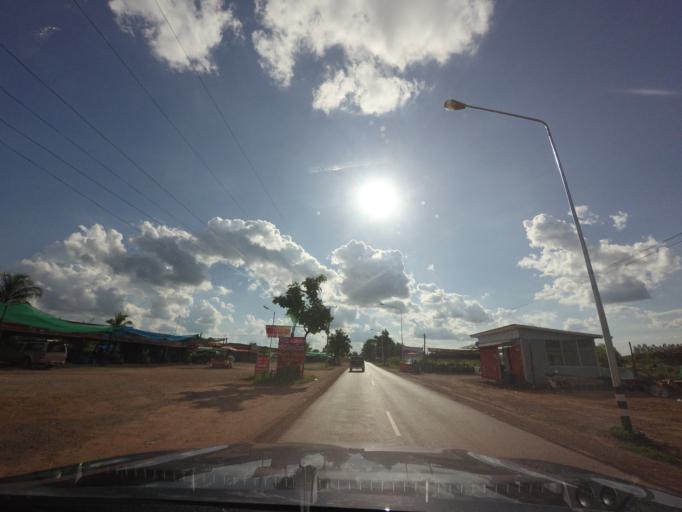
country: TH
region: Changwat Udon Thani
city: Ban Dung
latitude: 17.7407
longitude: 103.3533
